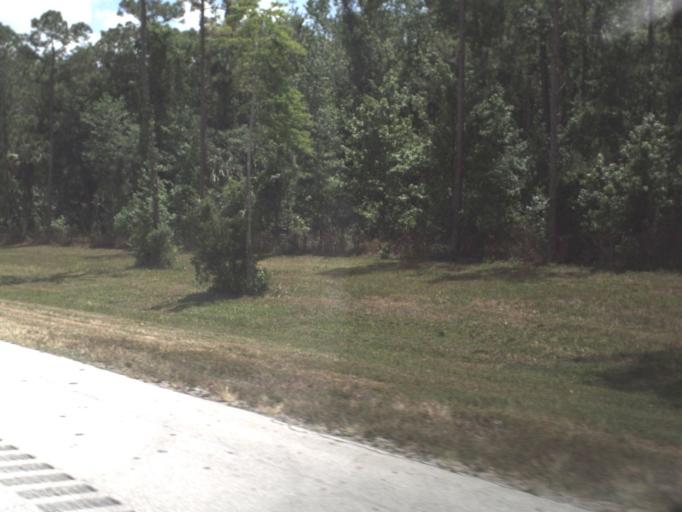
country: US
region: Florida
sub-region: Orange County
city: Christmas
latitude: 28.4524
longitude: -80.9870
